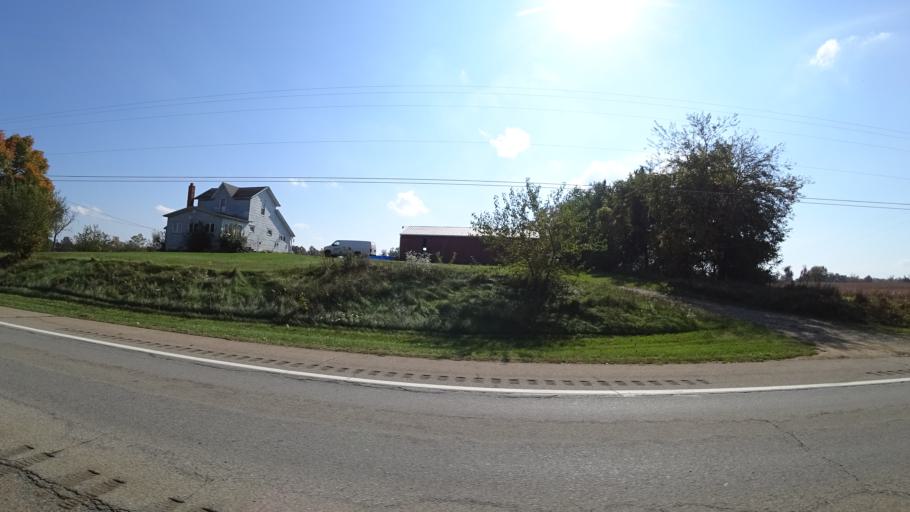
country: US
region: Michigan
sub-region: Calhoun County
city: Homer
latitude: 42.1624
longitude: -84.7261
